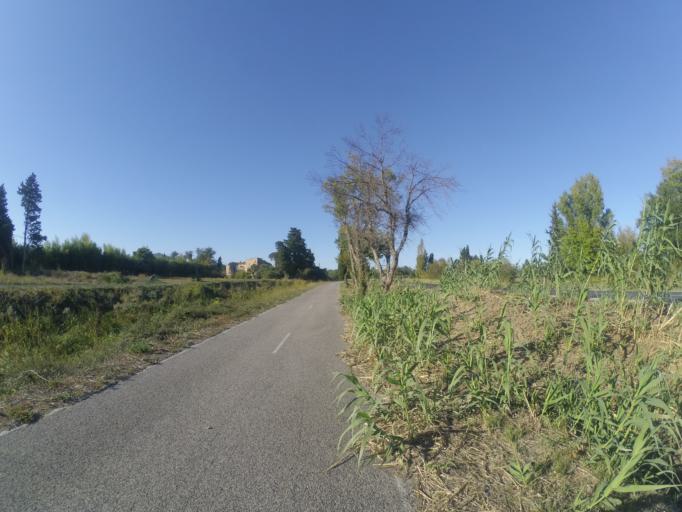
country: FR
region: Languedoc-Roussillon
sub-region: Departement des Pyrenees-Orientales
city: Pezilla-la-Riviere
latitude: 42.6891
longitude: 2.7522
